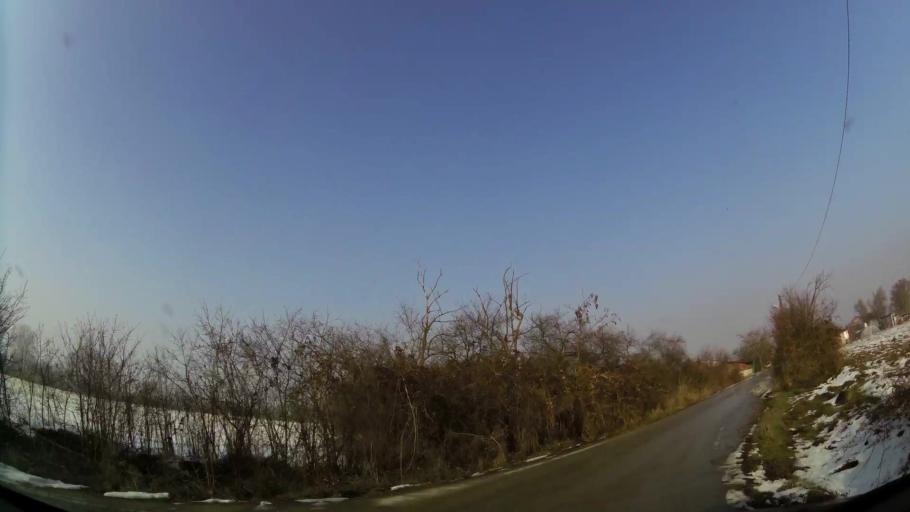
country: MK
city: Kadino
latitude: 41.9656
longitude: 21.5933
